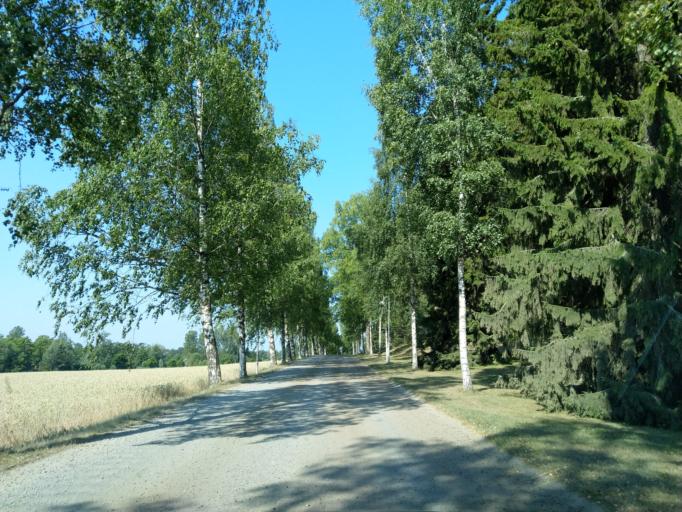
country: FI
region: Satakunta
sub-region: Pori
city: Noormarkku
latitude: 61.5952
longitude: 21.8729
